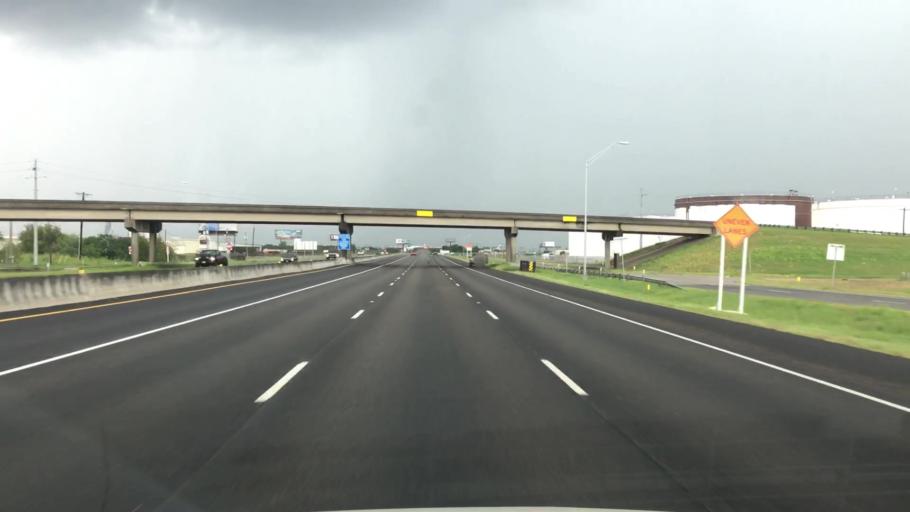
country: US
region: Texas
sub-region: Nueces County
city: Corpus Christi
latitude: 27.8109
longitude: -97.5016
